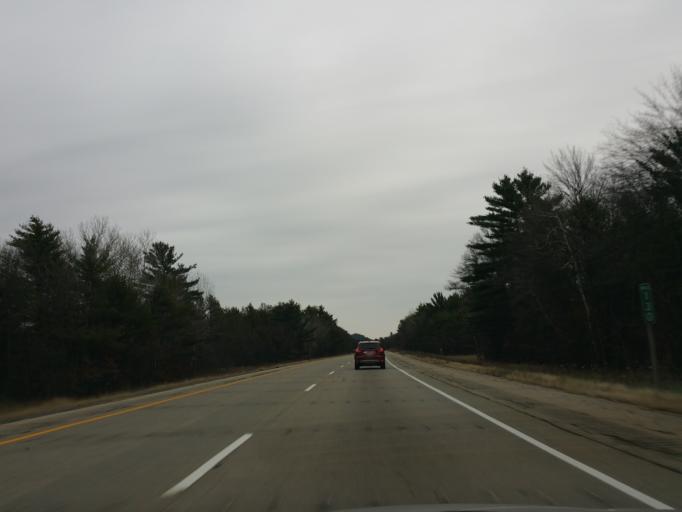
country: US
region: Wisconsin
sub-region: Monroe County
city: Tomah
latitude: 44.1808
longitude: -90.6134
